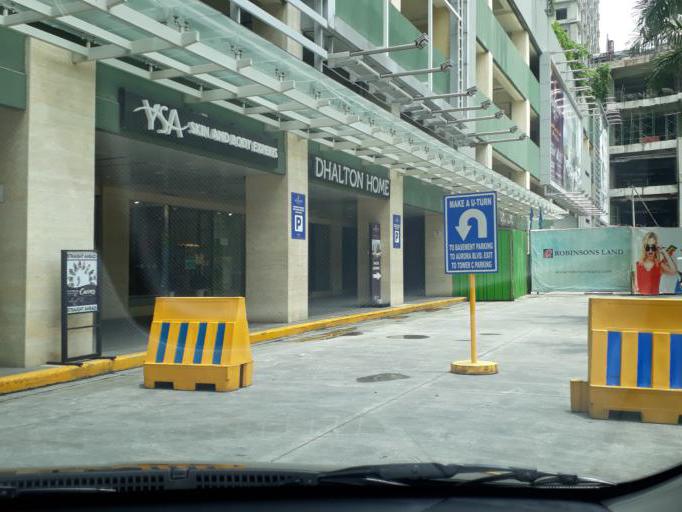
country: PH
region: Metro Manila
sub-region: San Juan
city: San Juan
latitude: 14.6148
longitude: 121.0389
